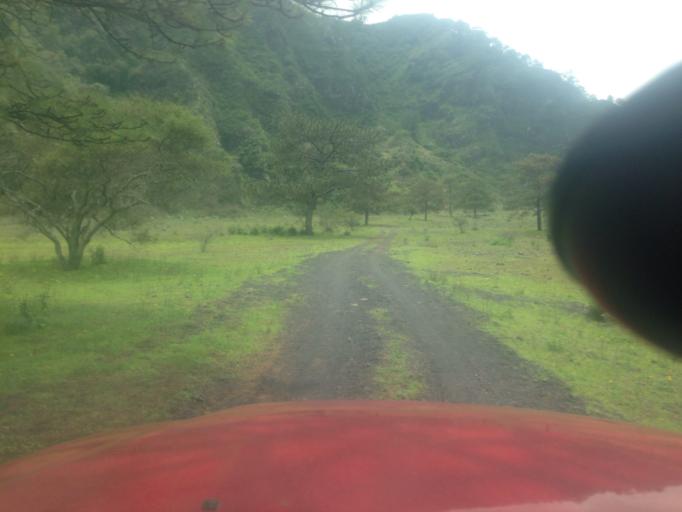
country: MX
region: Nayarit
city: Jala
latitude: 21.1168
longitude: -104.5015
